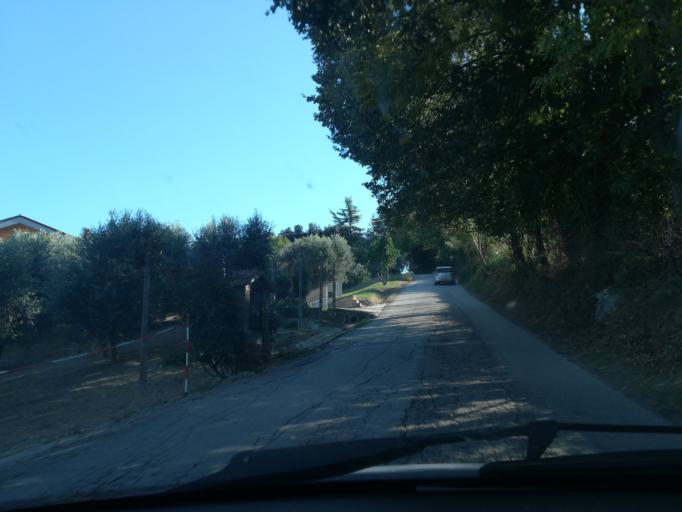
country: IT
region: The Marches
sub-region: Provincia di Macerata
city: Macerata
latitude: 43.3045
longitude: 13.4783
